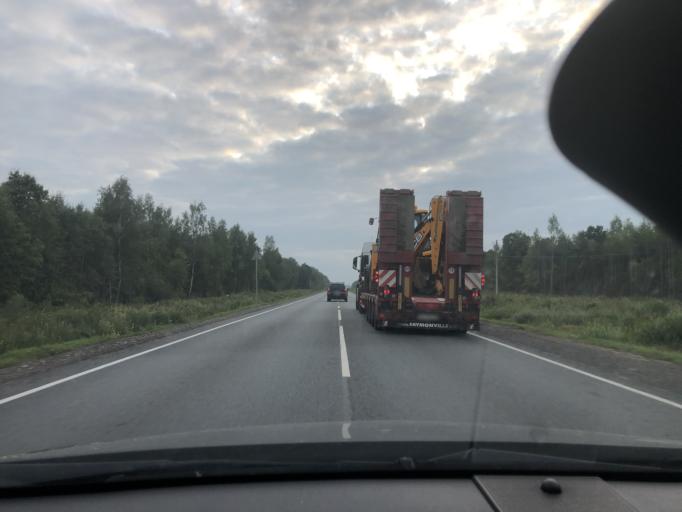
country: RU
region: Kaluga
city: Ferzikovo
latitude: 54.3590
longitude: 36.7631
